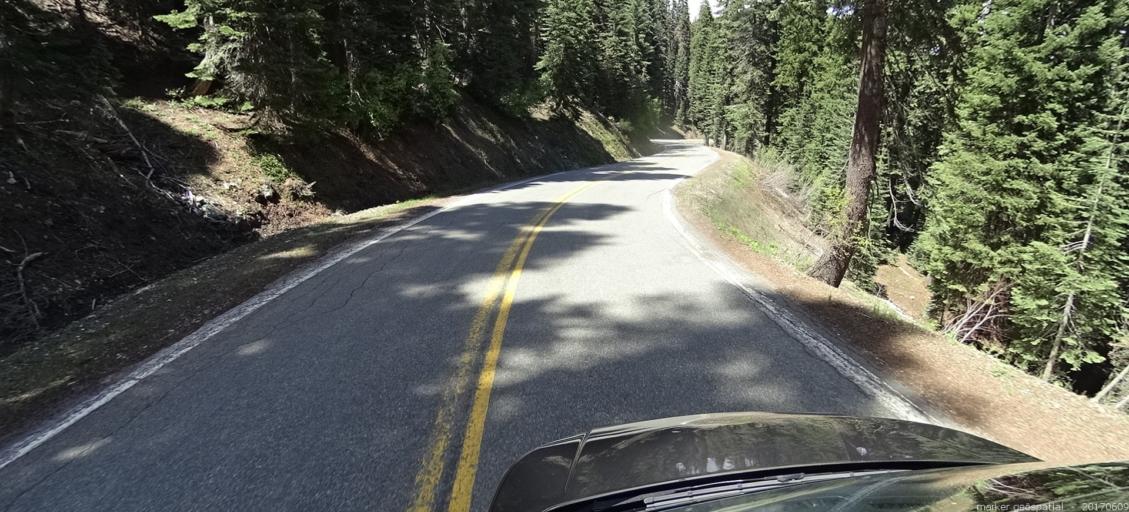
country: US
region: California
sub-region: Siskiyou County
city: Yreka
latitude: 41.3990
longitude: -122.9968
